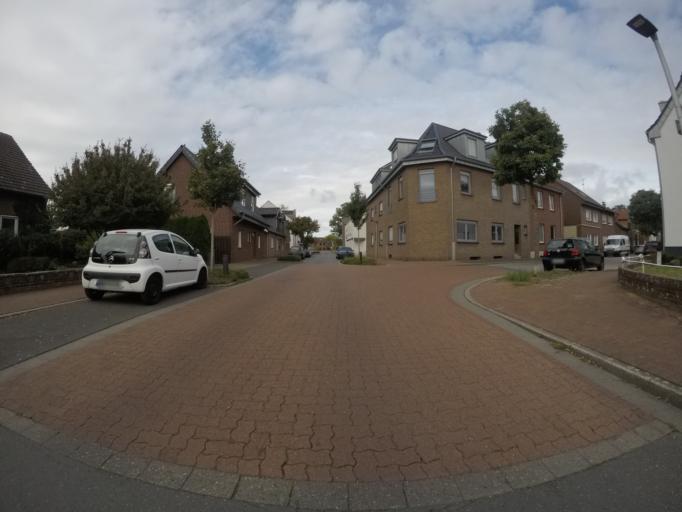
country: DE
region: North Rhine-Westphalia
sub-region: Regierungsbezirk Dusseldorf
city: Bocholt
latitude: 51.8398
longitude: 6.6294
